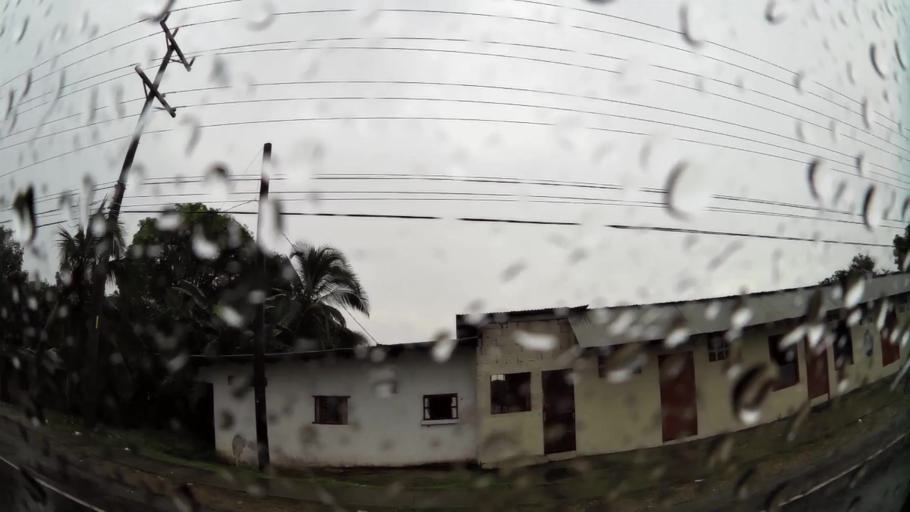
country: PA
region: Colon
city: Puerto Pilon
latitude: 9.3574
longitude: -79.7974
